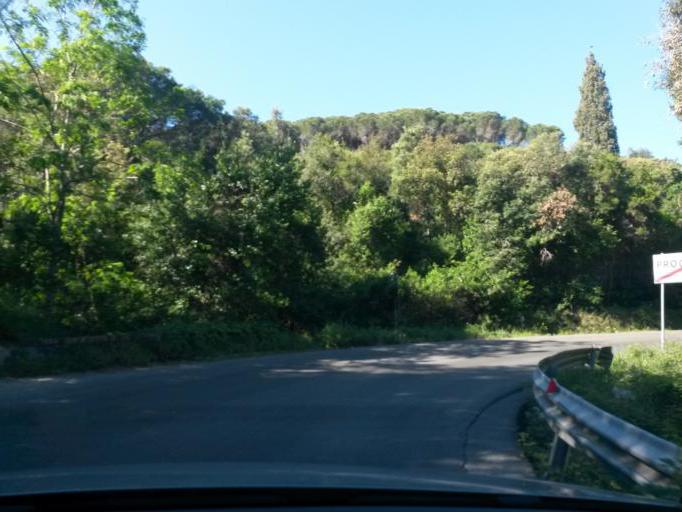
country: IT
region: Tuscany
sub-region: Provincia di Livorno
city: Campo nell'Elba
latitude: 42.7850
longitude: 10.2380
